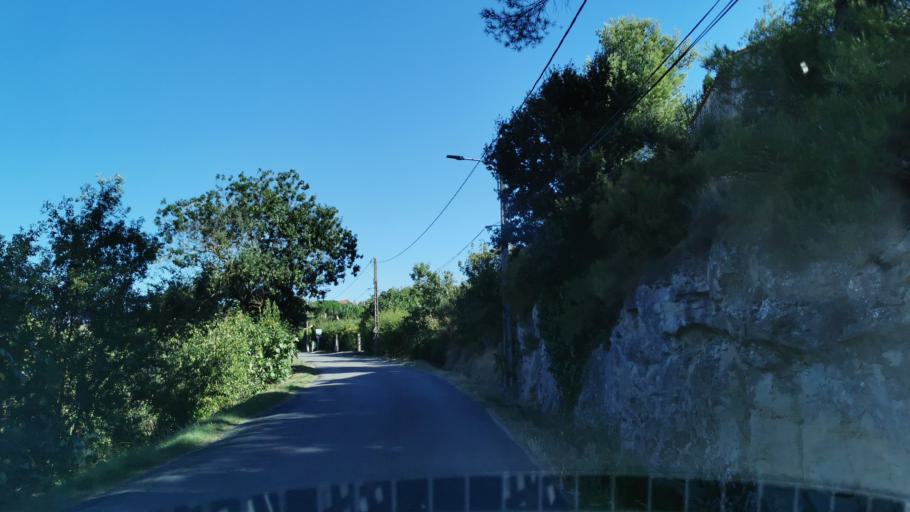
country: FR
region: Languedoc-Roussillon
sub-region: Departement de l'Aude
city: Conques-sur-Orbiel
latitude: 43.2494
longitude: 2.4393
